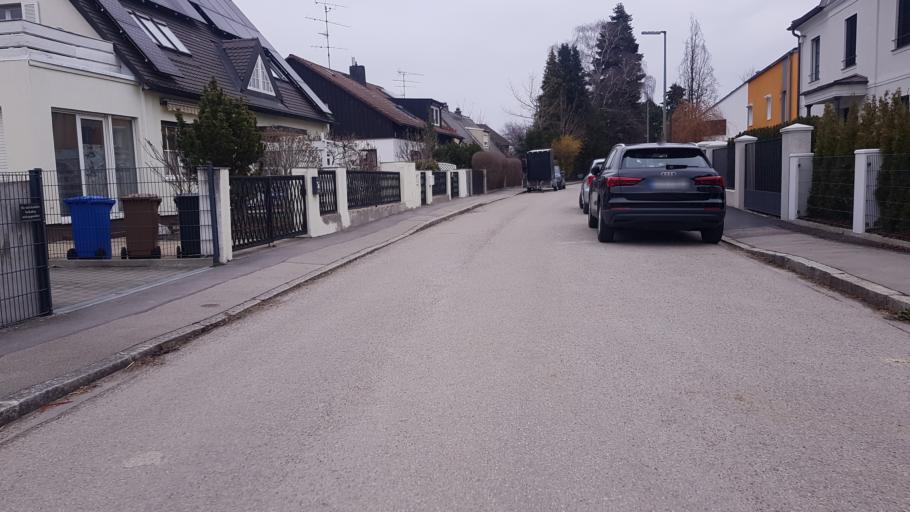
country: DE
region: Bavaria
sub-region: Upper Bavaria
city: Bogenhausen
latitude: 48.1422
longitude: 11.6306
